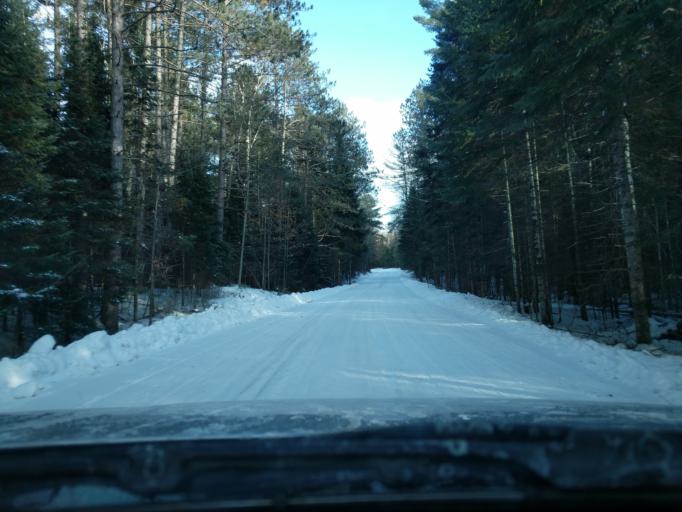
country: US
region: Wisconsin
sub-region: Vilas County
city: Eagle River
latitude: 45.8113
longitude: -89.0478
